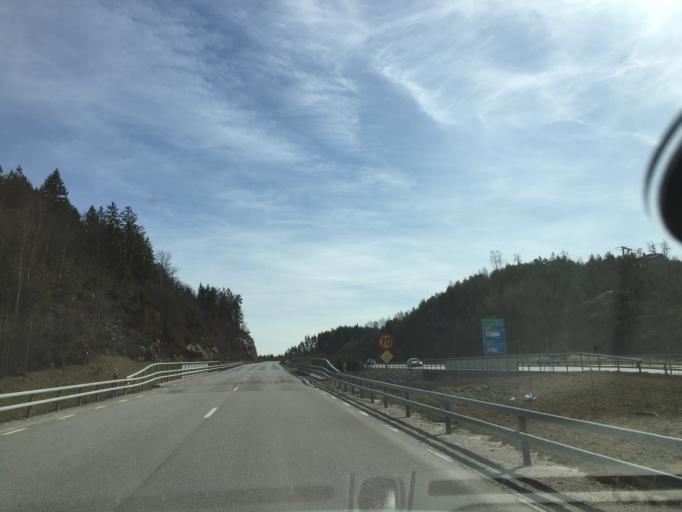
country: SE
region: Vaestra Goetaland
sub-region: Uddevalla Kommun
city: Uddevalla
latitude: 58.3698
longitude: 11.7933
